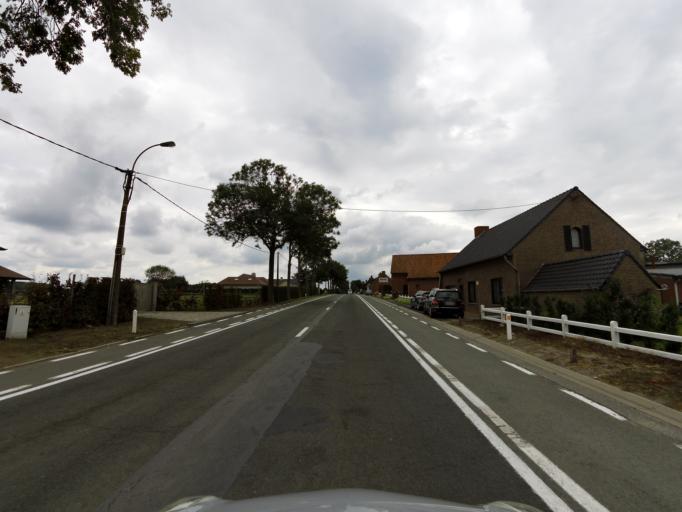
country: BE
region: Flanders
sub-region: Provincie West-Vlaanderen
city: Ichtegem
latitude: 51.0950
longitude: 3.0423
